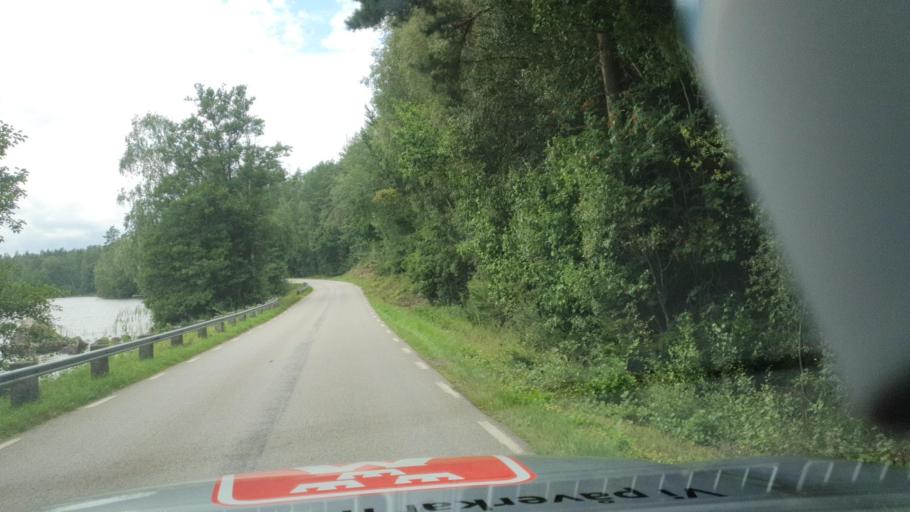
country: SE
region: Blekinge
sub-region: Ronneby Kommun
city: Brakne-Hoby
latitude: 56.3489
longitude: 15.1809
